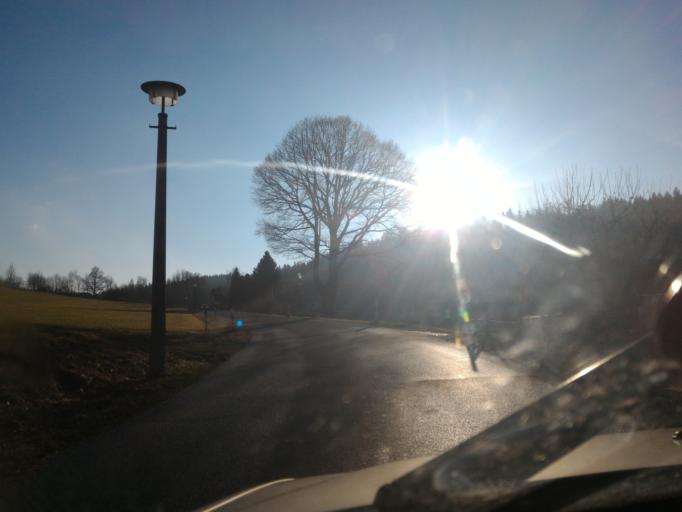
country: DE
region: Saxony
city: Kurort Jonsdorf
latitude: 50.8514
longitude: 14.7040
